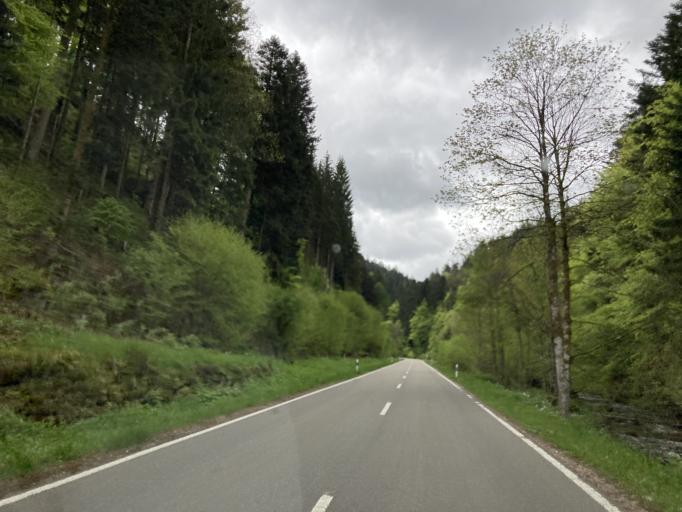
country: DE
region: Baden-Wuerttemberg
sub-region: Freiburg Region
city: Schonach im Schwarzwald
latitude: 48.1664
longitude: 8.1580
